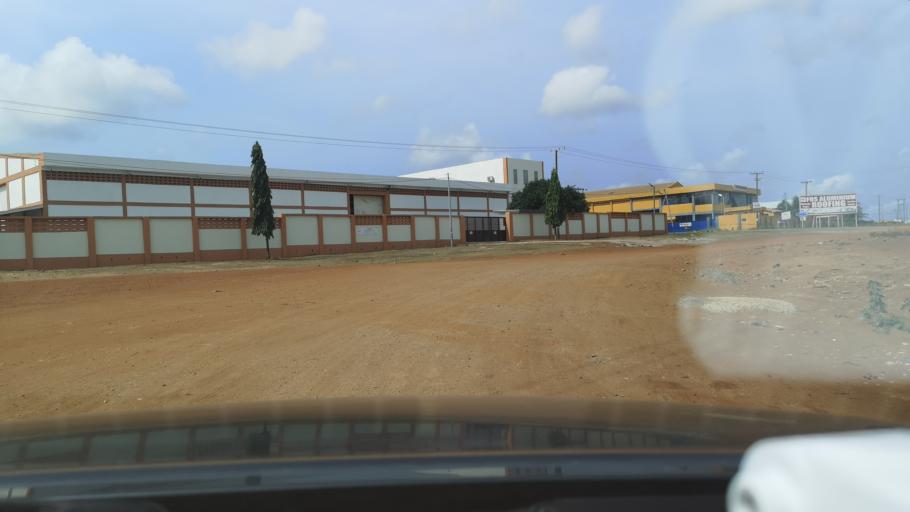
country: GH
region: Greater Accra
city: Tema
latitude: 5.6798
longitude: -0.0307
